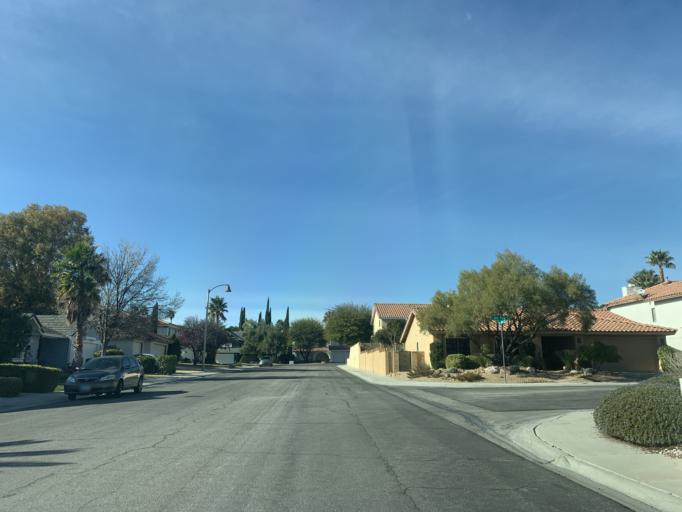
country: US
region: Nevada
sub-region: Clark County
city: Summerlin South
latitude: 36.1344
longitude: -115.2918
